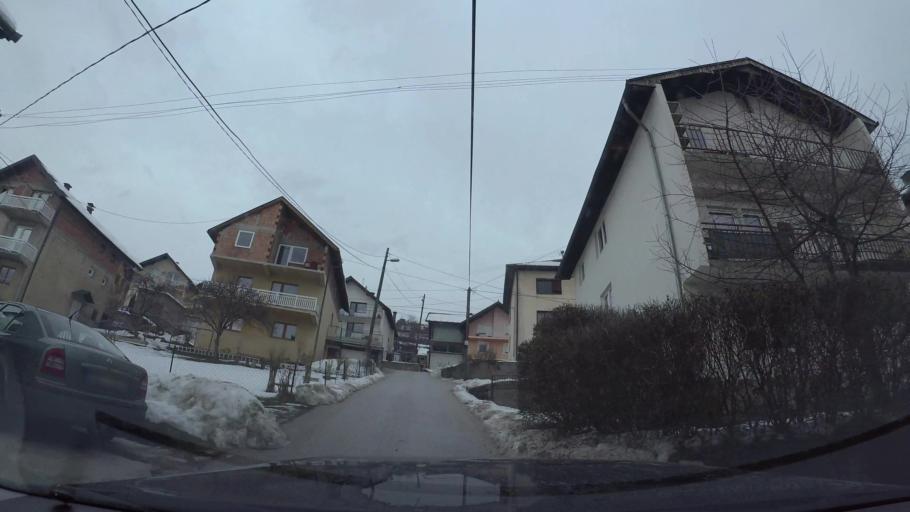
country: BA
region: Federation of Bosnia and Herzegovina
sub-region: Kanton Sarajevo
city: Sarajevo
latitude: 43.8631
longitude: 18.3582
